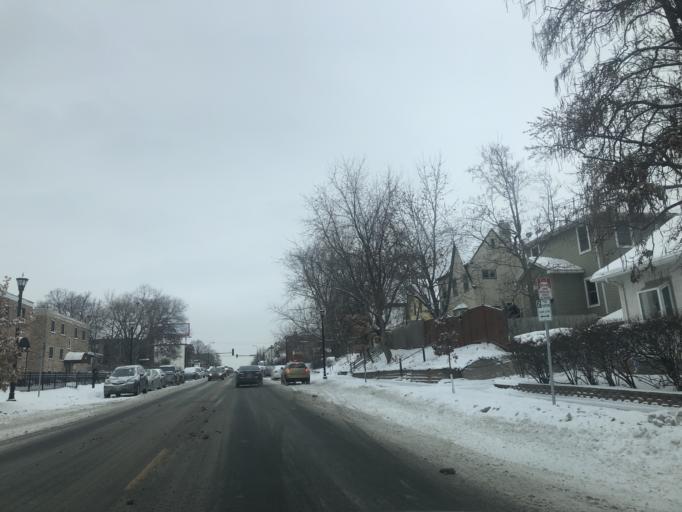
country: US
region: Minnesota
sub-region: Hennepin County
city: Richfield
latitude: 44.9324
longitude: -93.2779
